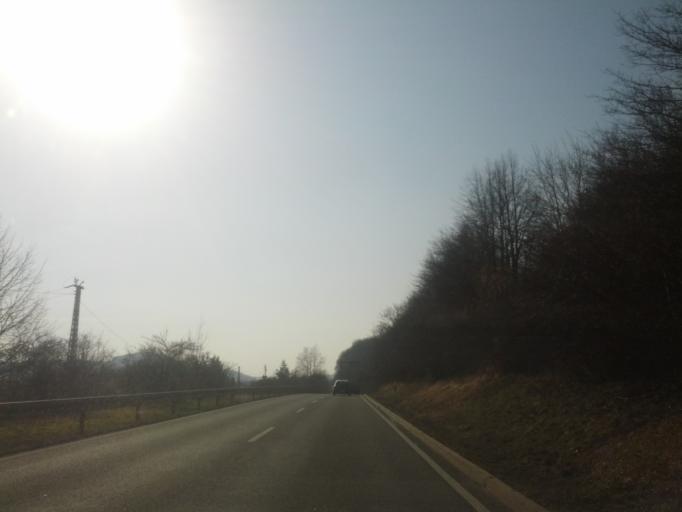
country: DE
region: Hesse
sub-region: Regierungsbezirk Kassel
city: Herleshausen
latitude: 51.0079
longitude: 10.2089
